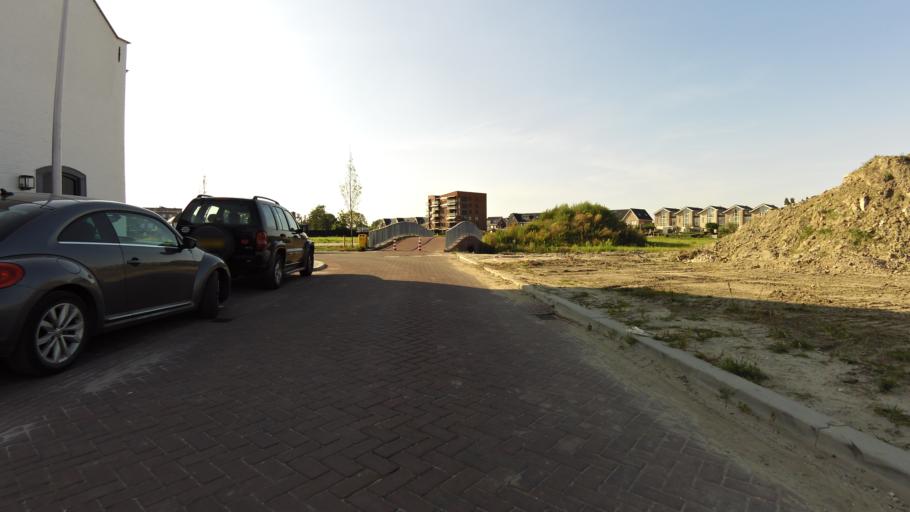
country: NL
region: South Holland
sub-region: Gemeente Katwijk
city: Rijnsburg
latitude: 52.1947
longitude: 4.4499
